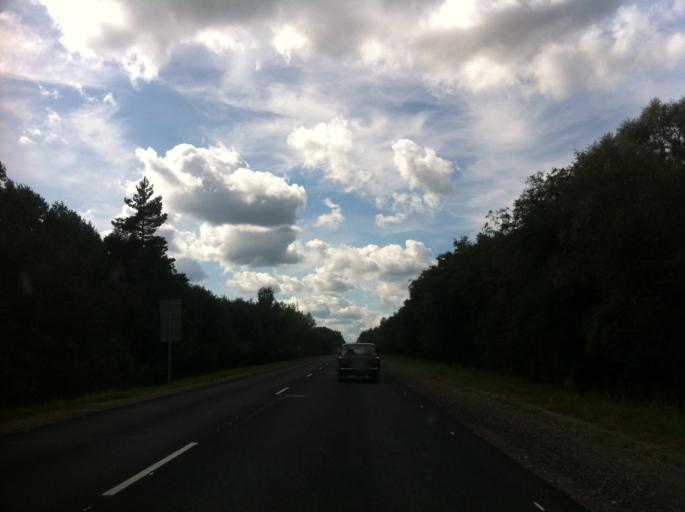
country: RU
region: Pskov
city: Izborsk
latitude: 57.7150
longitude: 27.9129
